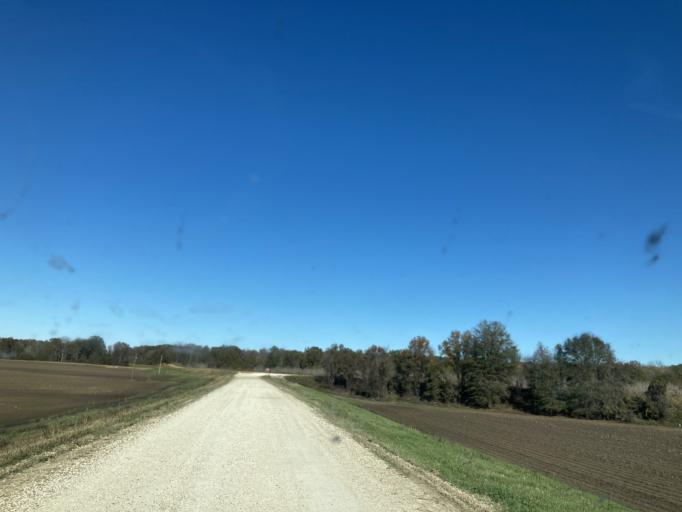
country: US
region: Mississippi
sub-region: Yazoo County
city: Yazoo City
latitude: 32.7760
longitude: -90.6391
